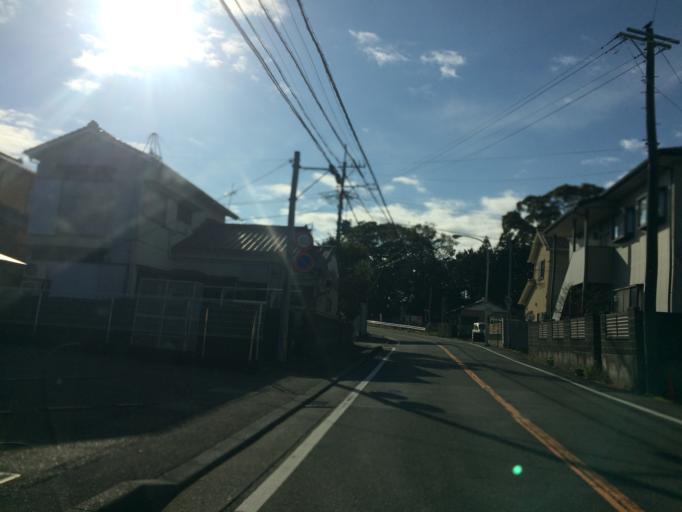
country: JP
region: Shizuoka
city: Shizuoka-shi
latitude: 34.9831
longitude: 138.4280
